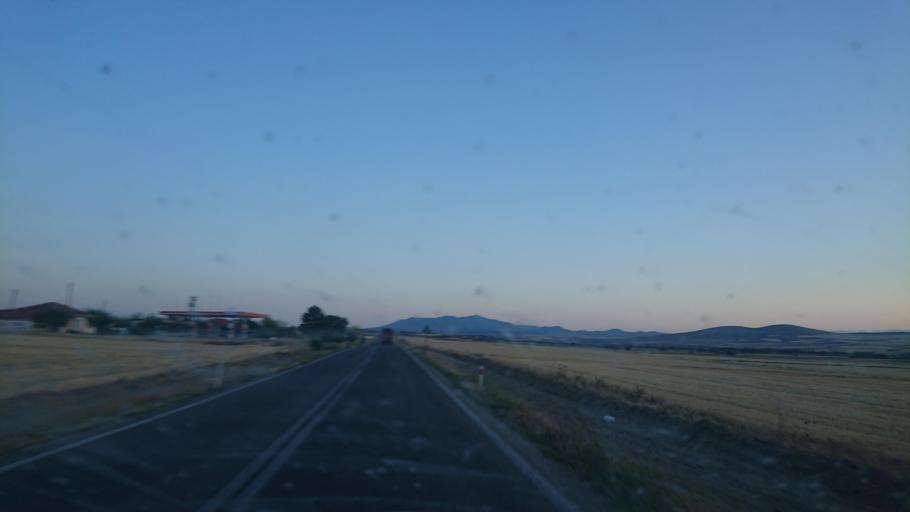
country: TR
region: Aksaray
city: Balci
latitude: 38.8248
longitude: 34.1366
